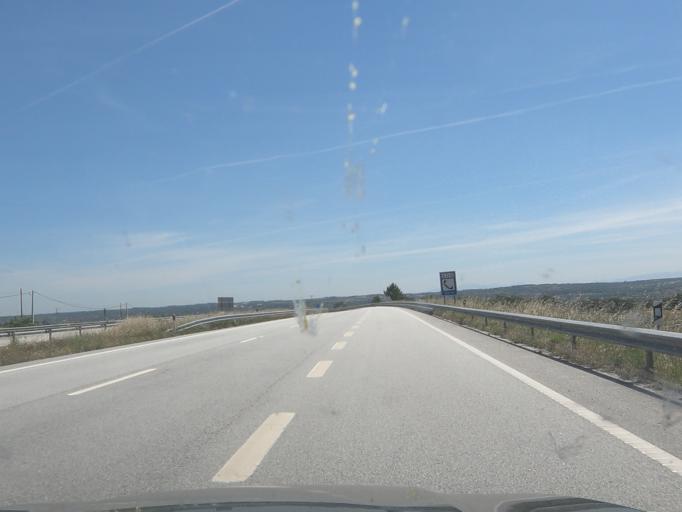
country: ES
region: Castille and Leon
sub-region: Provincia de Salamanca
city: Fuentes de Onoro
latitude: 40.6042
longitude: -6.9495
